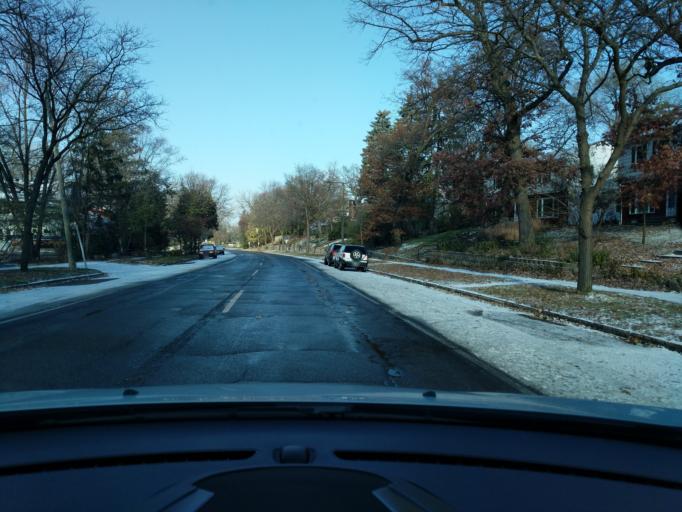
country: US
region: Minnesota
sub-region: Ramsey County
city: Lauderdale
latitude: 44.9848
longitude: -93.1981
